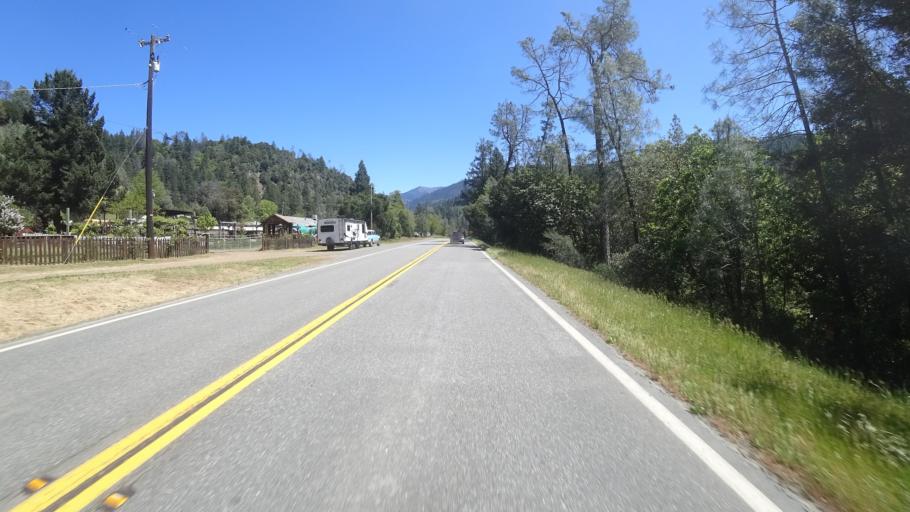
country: US
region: California
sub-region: Trinity County
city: Hayfork
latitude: 40.7412
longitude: -123.2562
